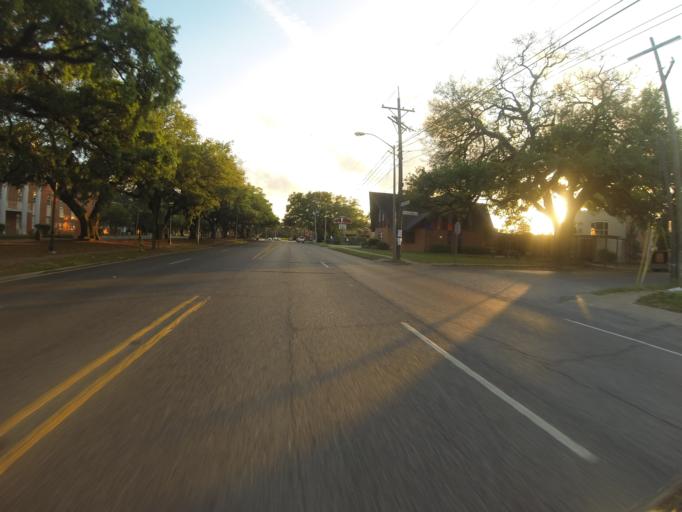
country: US
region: Louisiana
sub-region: Lafayette Parish
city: Lafayette
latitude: 30.2158
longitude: -92.0206
